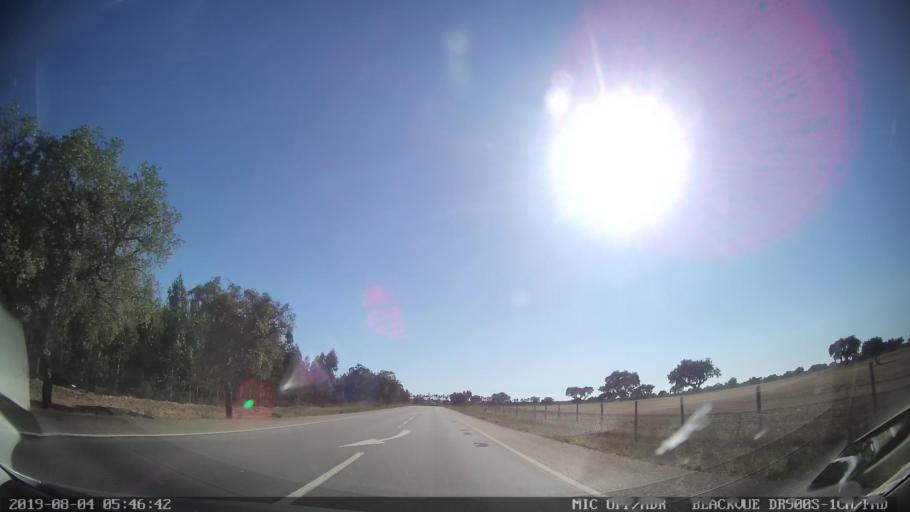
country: PT
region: Portalegre
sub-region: Gaviao
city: Gaviao
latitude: 39.4479
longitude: -7.7920
